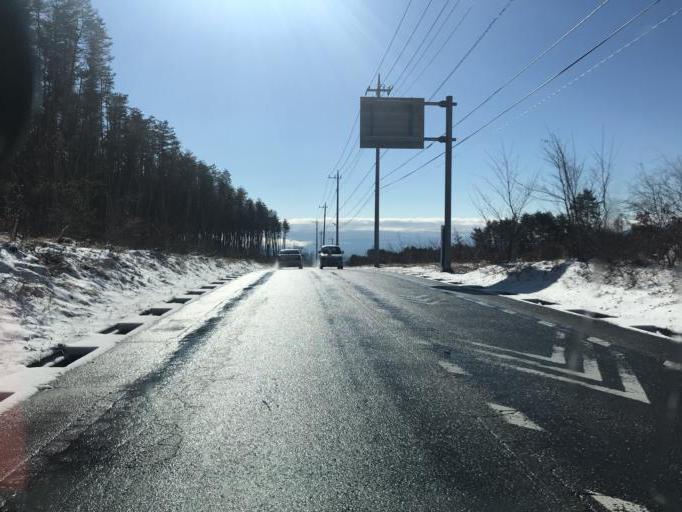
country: JP
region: Yamanashi
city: Nirasaki
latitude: 35.8683
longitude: 138.3329
